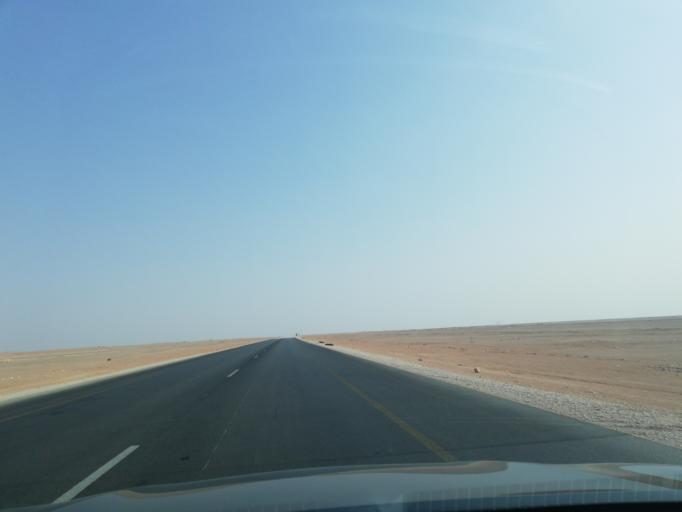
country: OM
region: Zufar
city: Salalah
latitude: 17.8647
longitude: 54.0069
